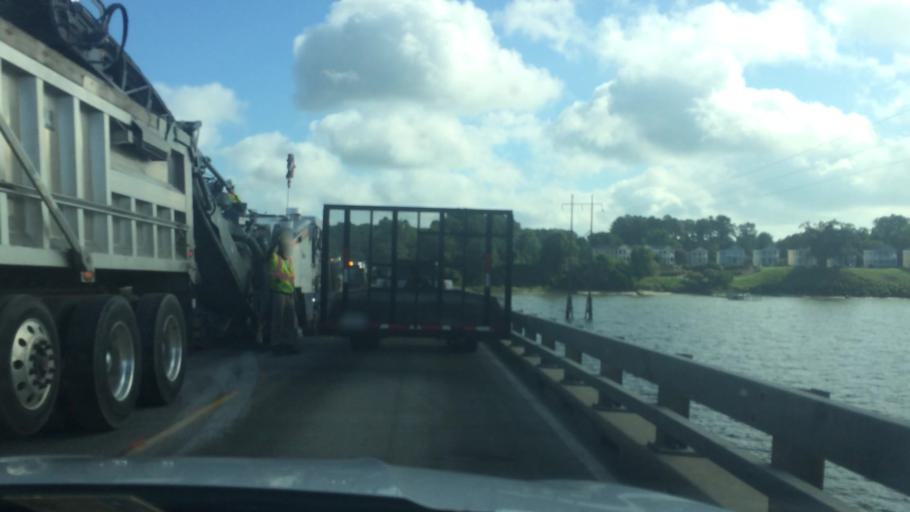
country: US
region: Virginia
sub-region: Lancaster County
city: Kilmarnock
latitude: 37.6335
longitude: -76.4139
